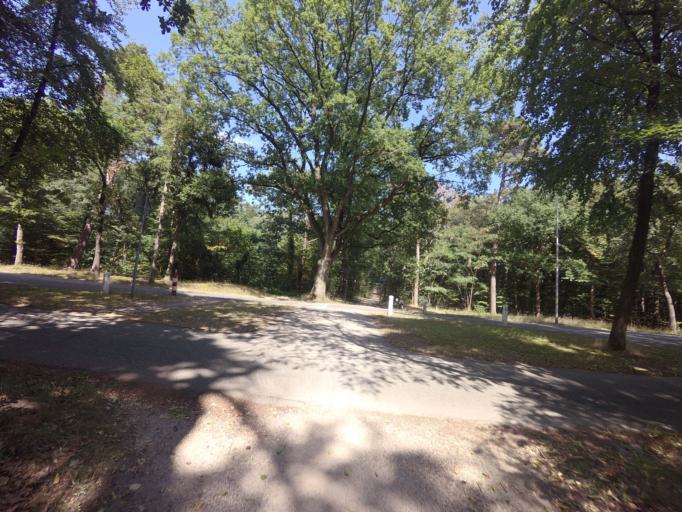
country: NL
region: Utrecht
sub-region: Gemeente Zeist
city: Zeist
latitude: 52.0848
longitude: 5.2664
